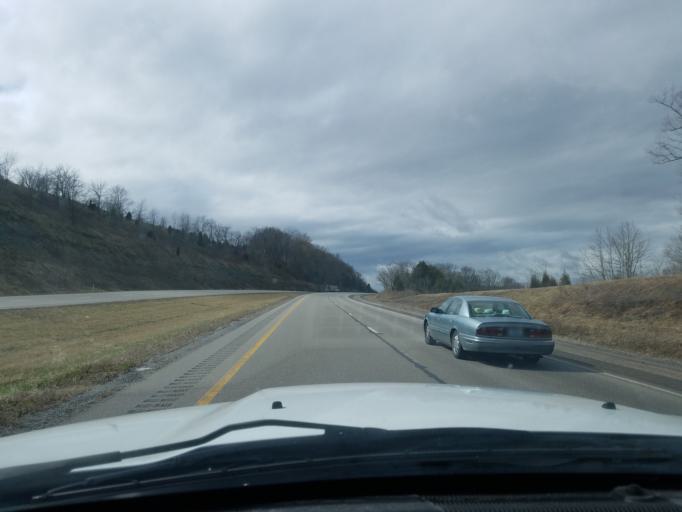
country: US
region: Kentucky
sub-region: Bath County
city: Owingsville
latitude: 38.1240
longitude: -83.7796
